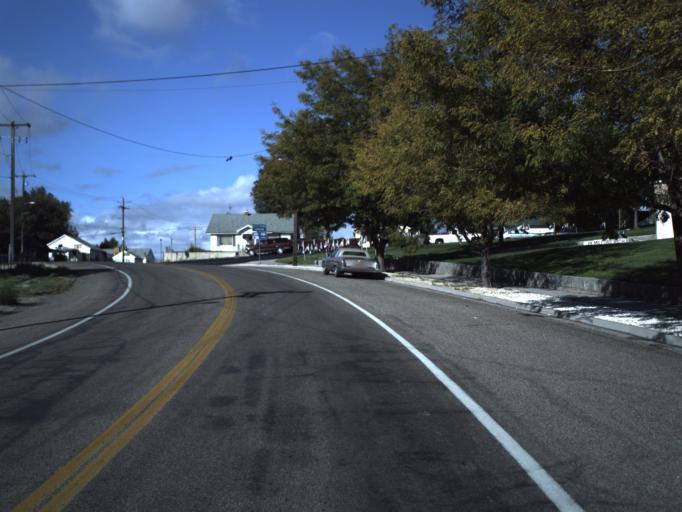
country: US
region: Utah
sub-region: Beaver County
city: Milford
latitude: 38.3973
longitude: -113.0133
